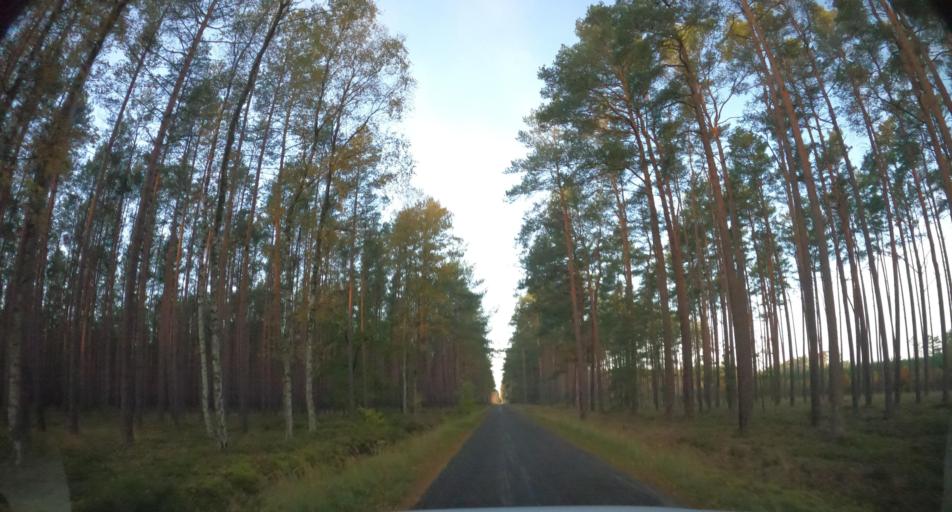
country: PL
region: West Pomeranian Voivodeship
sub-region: Powiat policki
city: Nowe Warpno
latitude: 53.6435
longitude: 14.3588
